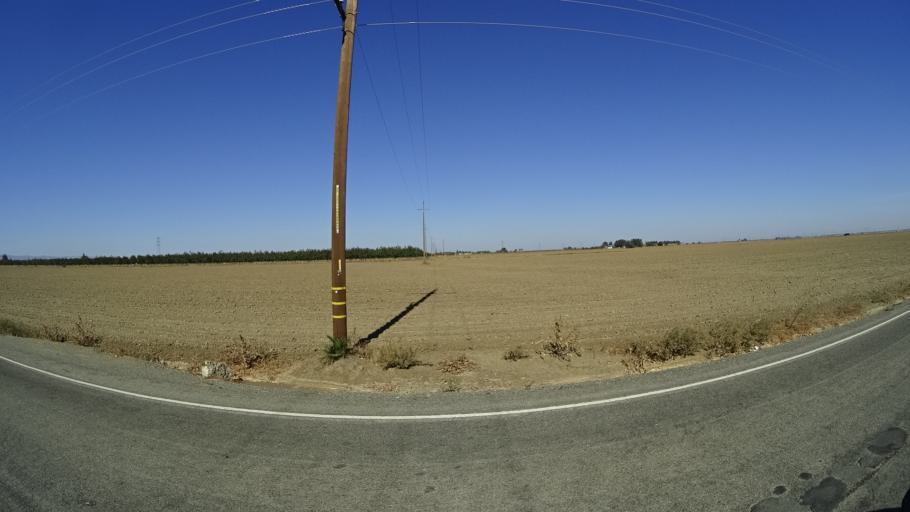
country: US
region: California
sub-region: Yolo County
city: Cottonwood
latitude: 38.6205
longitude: -121.9619
